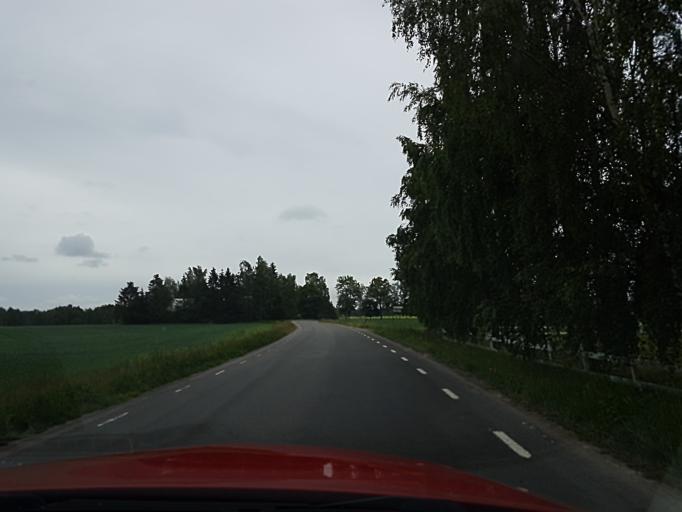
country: SE
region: Vaestra Goetaland
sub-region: Skovde Kommun
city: Skoevde
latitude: 58.3725
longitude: 13.9305
